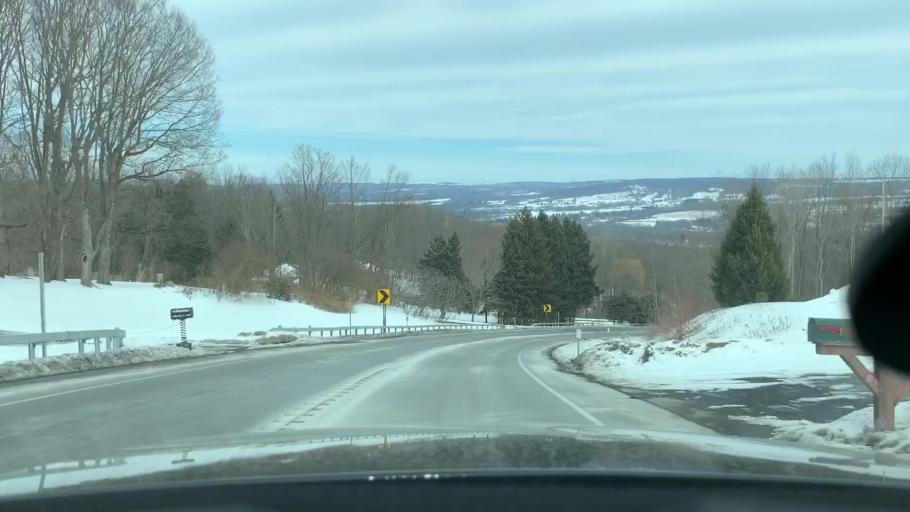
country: US
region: New York
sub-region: Herkimer County
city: Frankfort
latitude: 43.0362
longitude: -75.1008
